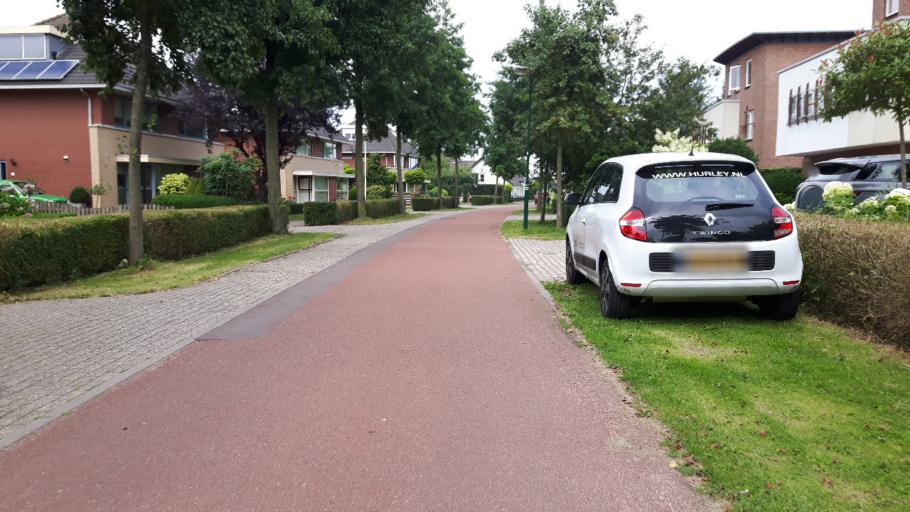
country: NL
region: Utrecht
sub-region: Gemeente Houten
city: Houten
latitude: 52.0244
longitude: 5.1846
